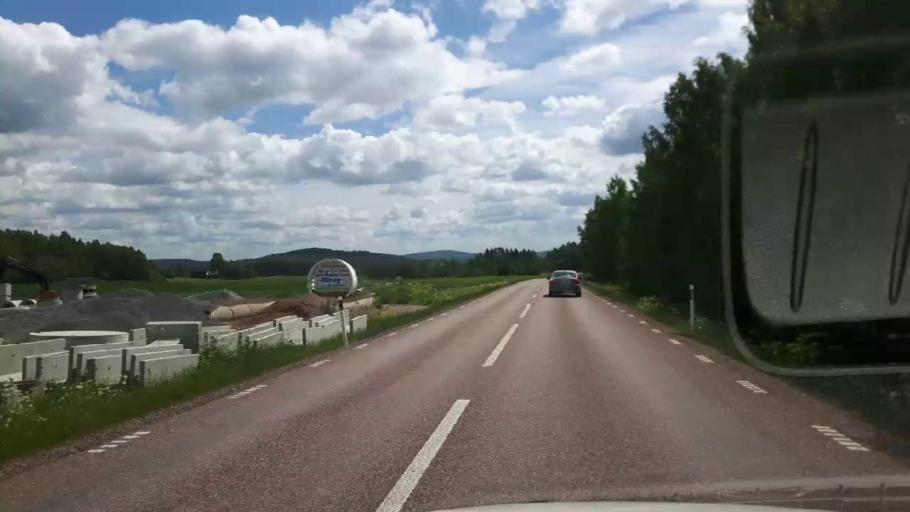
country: SE
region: Dalarna
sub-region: Saters Kommun
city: Saeter
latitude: 60.4267
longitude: 15.8366
